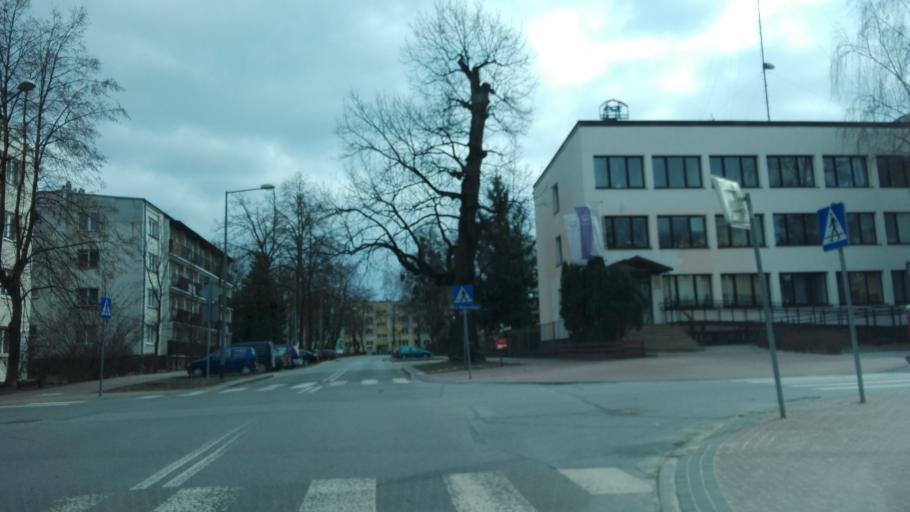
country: PL
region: Lublin Voivodeship
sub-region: Powiat pulawski
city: Pulawy
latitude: 51.4191
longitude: 21.9793
